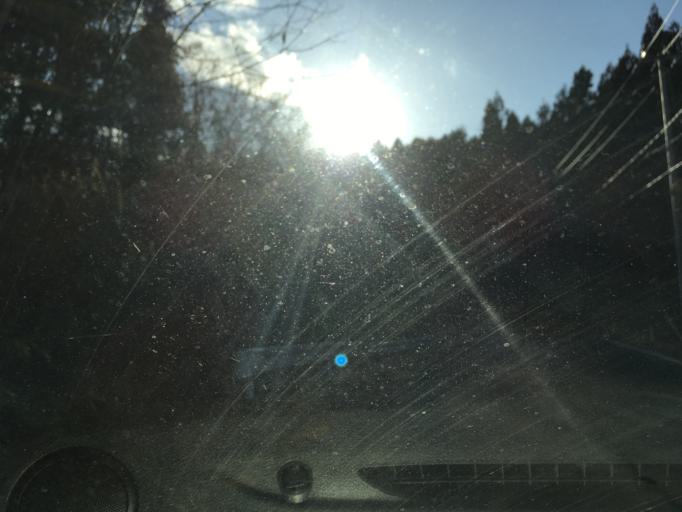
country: JP
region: Iwate
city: Ichinoseki
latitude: 38.8133
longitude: 140.9975
